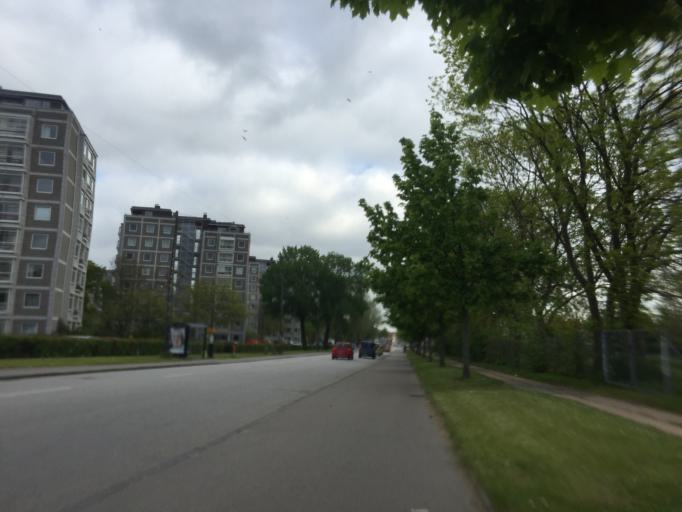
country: DK
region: Capital Region
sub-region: Frederiksberg Kommune
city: Frederiksberg
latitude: 55.7036
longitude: 12.5129
